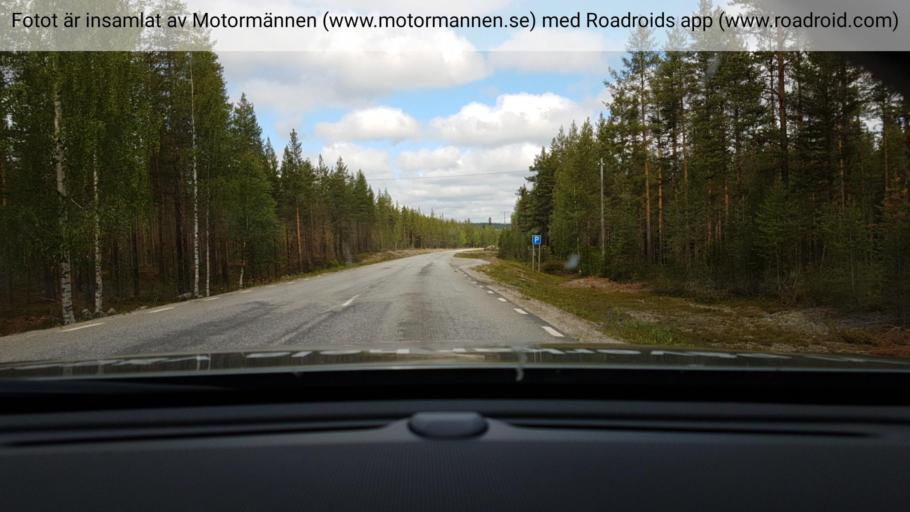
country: SE
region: Vaesterbotten
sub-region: Lycksele Kommun
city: Lycksele
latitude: 64.8579
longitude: 18.7315
